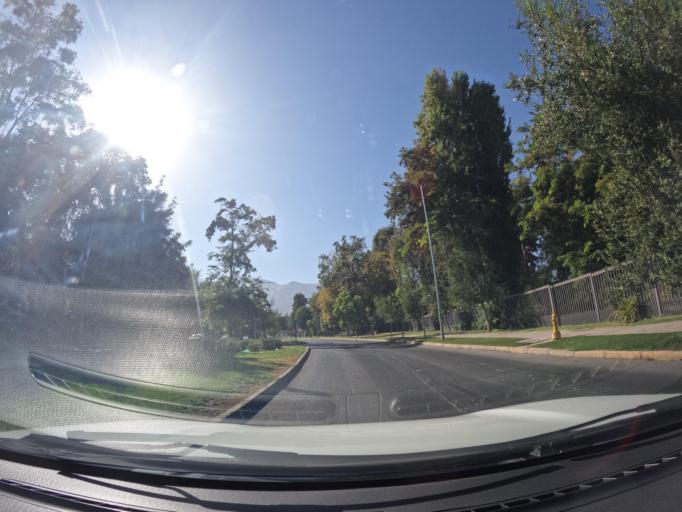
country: CL
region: Santiago Metropolitan
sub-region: Provincia de Santiago
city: Villa Presidente Frei, Nunoa, Santiago, Chile
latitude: -33.4981
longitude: -70.5677
